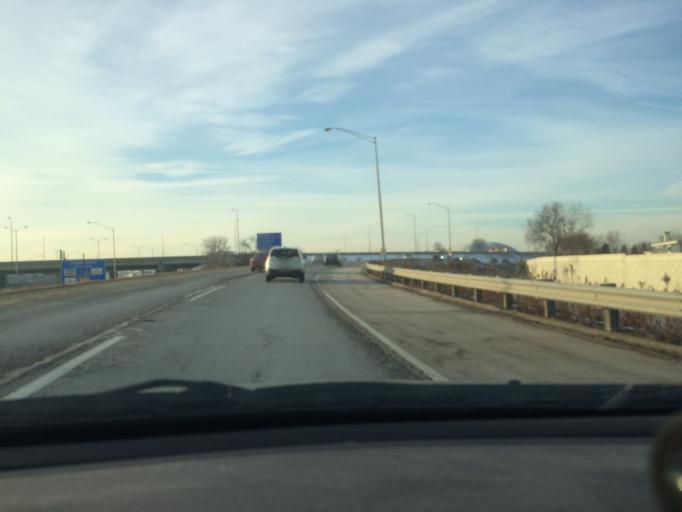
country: US
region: Illinois
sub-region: Cook County
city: Rosemont
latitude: 41.9862
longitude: -87.8698
